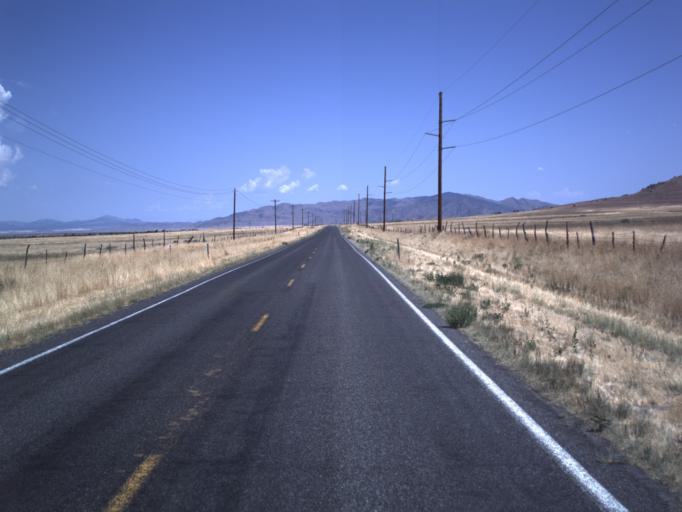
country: US
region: Utah
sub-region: Millard County
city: Delta
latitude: 39.4170
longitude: -112.3294
